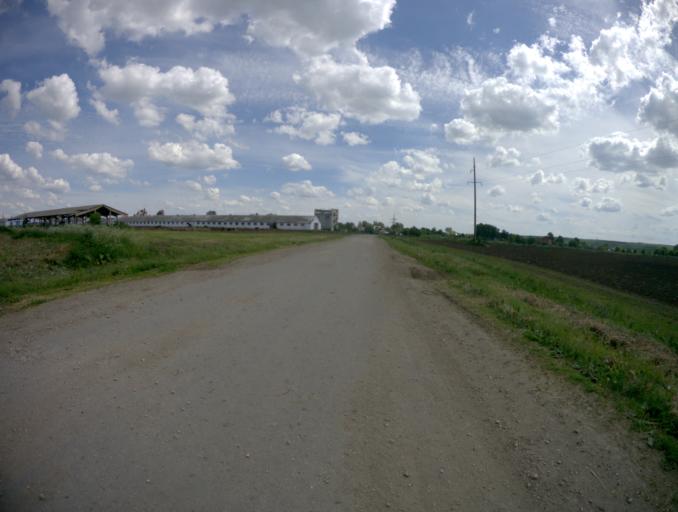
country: RU
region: Vladimir
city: Stavrovo
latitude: 56.3622
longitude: 39.9779
